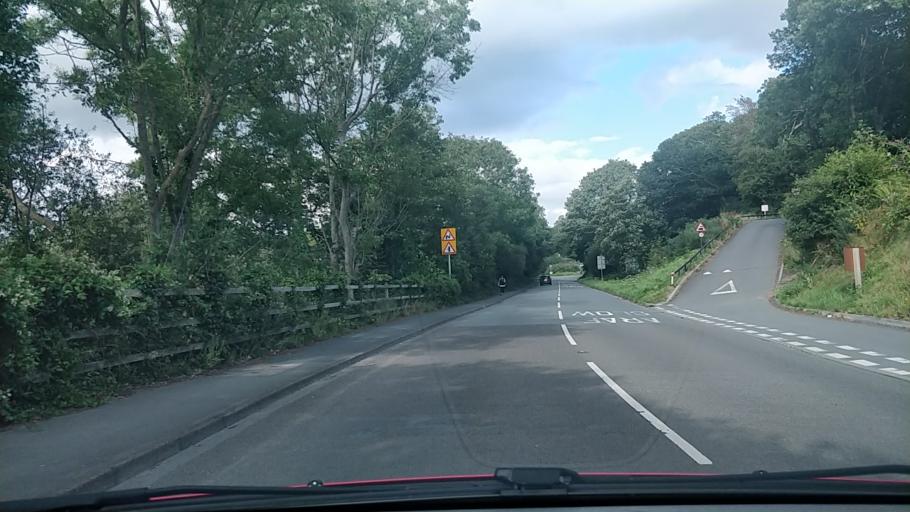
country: GB
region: Wales
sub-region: Gwynedd
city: Porthmadog
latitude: 52.9209
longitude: -4.1055
